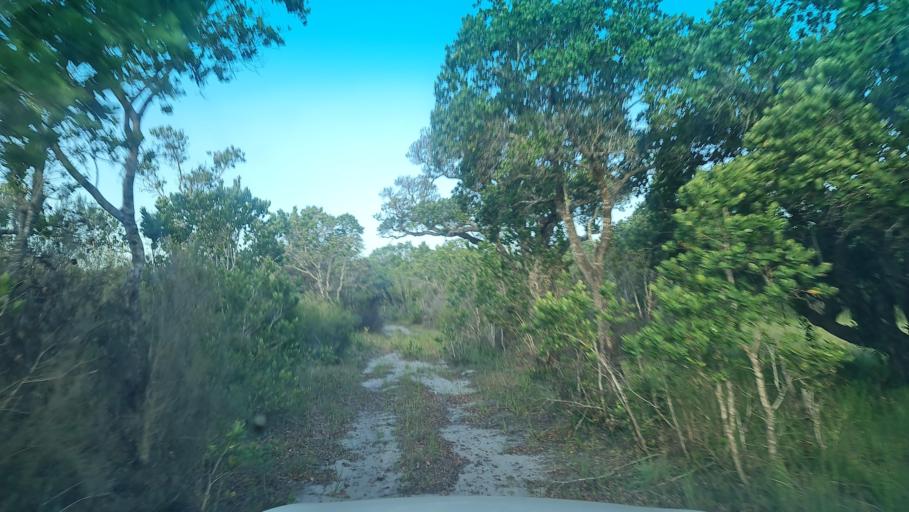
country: MZ
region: Gaza
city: Macia
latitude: -25.2263
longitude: 33.0241
